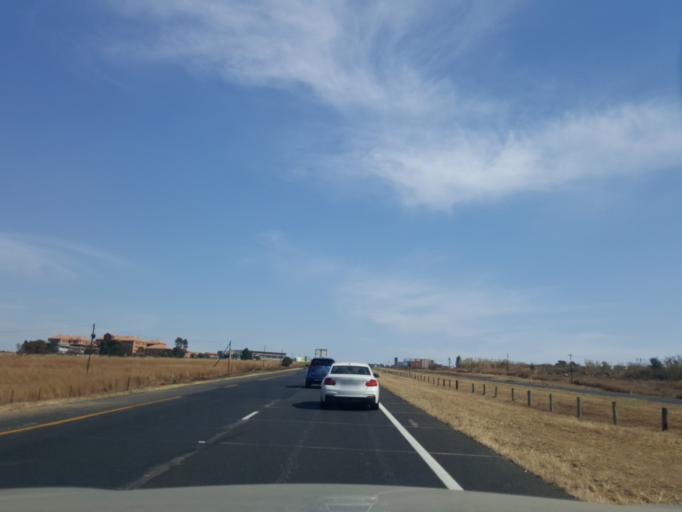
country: ZA
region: Mpumalanga
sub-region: Nkangala District Municipality
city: Witbank
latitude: -25.8822
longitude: 29.2812
